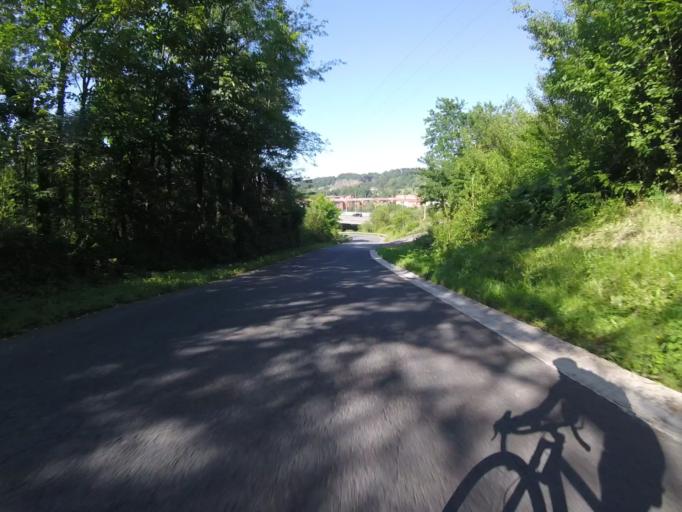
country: ES
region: Basque Country
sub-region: Provincia de Guipuzcoa
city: Astigarraga
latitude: 43.2917
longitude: -1.9584
